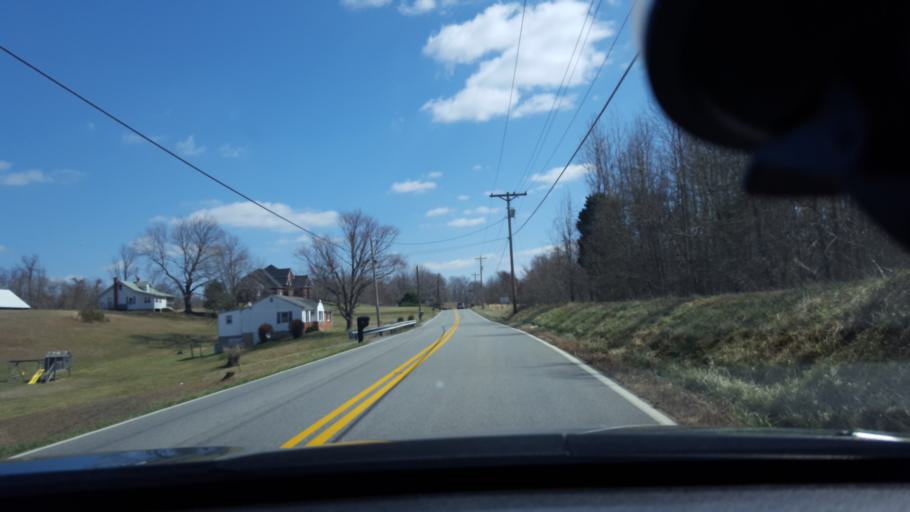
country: US
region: Maryland
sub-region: Calvert County
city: Huntingtown
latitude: 38.6276
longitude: -76.5599
